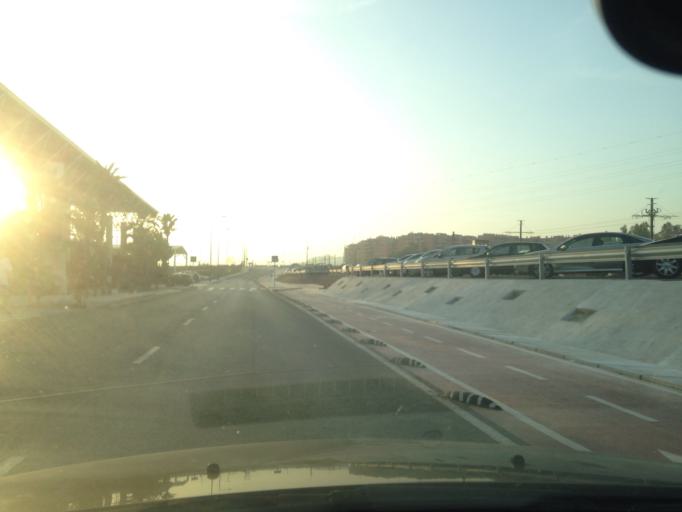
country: ES
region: Andalusia
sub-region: Provincia de Malaga
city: Malaga
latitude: 36.7163
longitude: -4.4803
